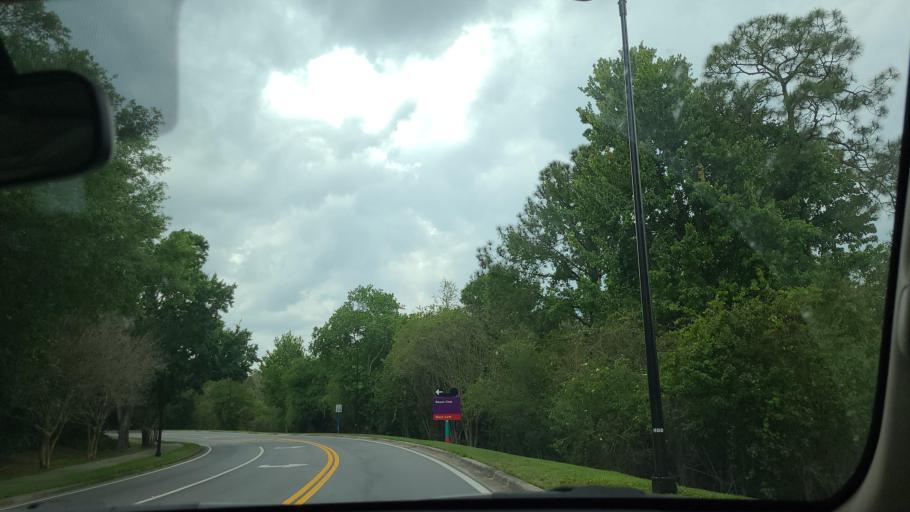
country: US
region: Florida
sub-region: Osceola County
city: Celebration
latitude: 28.3738
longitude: -81.5556
